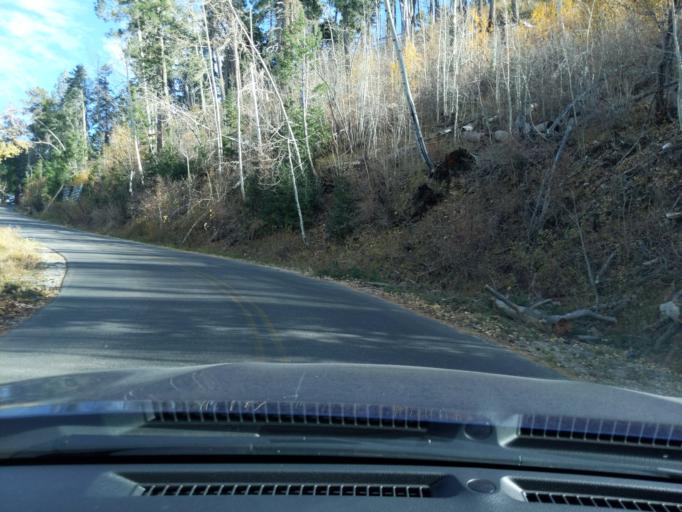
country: US
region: Arizona
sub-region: Pima County
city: Catalina
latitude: 32.4449
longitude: -110.7883
